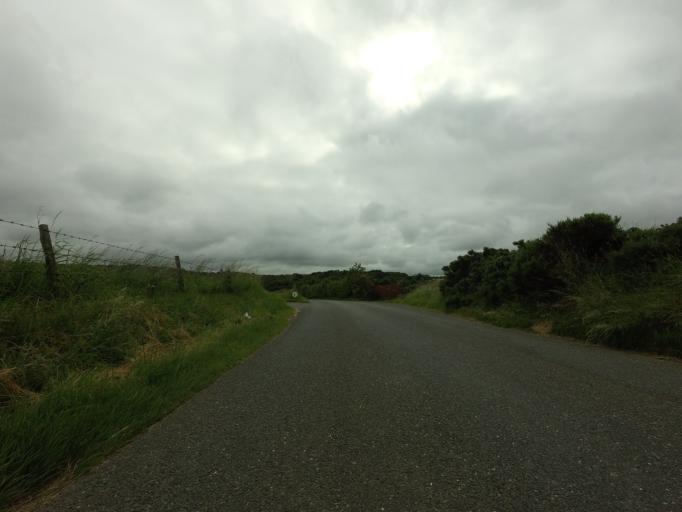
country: GB
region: Scotland
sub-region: Aberdeenshire
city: Turriff
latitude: 57.5337
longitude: -2.4215
